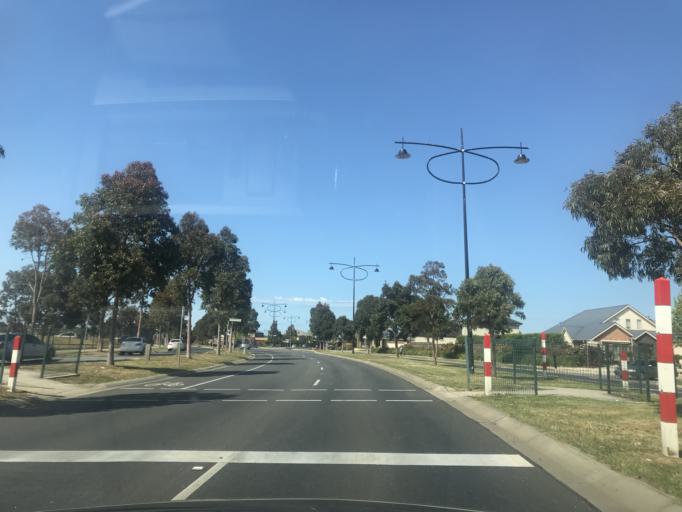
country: AU
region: Victoria
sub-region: Wyndham
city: Williams Landing
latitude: -37.8876
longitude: 144.7323
